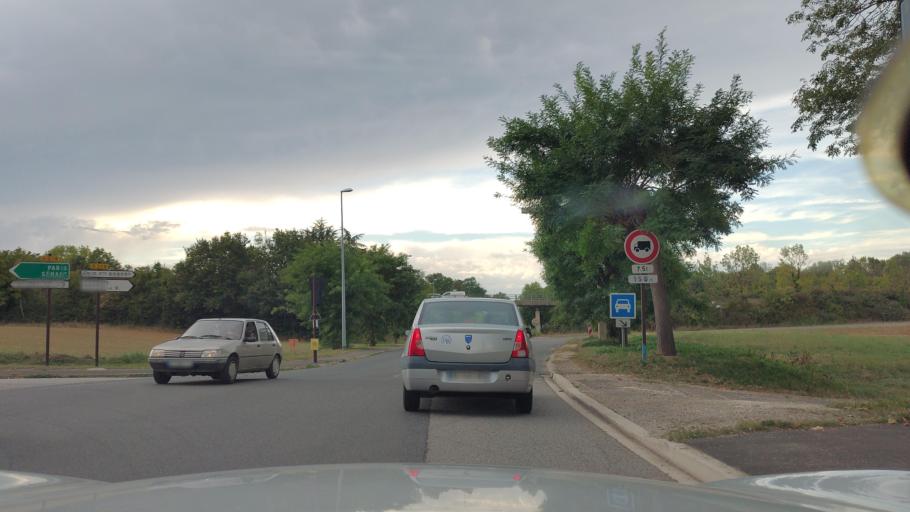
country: FR
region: Ile-de-France
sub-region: Departement de Seine-et-Marne
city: Guignes
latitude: 48.6379
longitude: 2.7938
